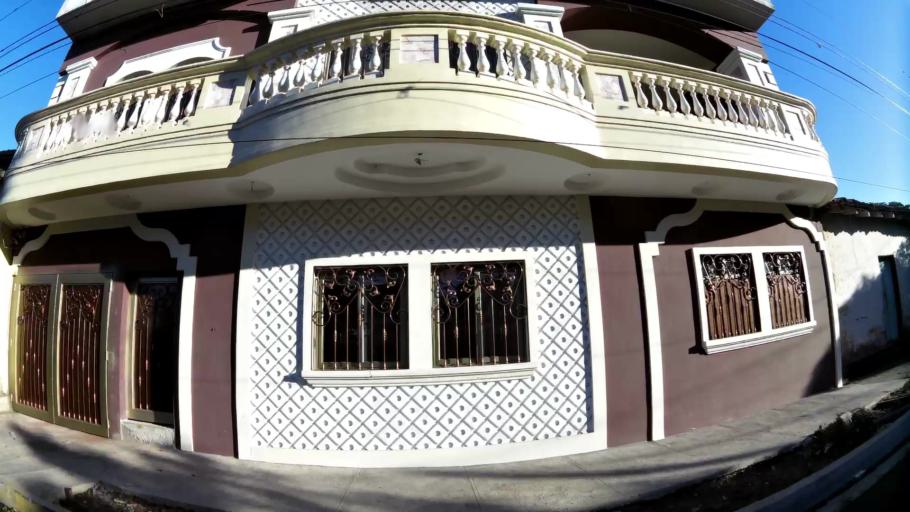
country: SV
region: San Miguel
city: San Miguel
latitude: 13.4868
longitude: -88.1811
